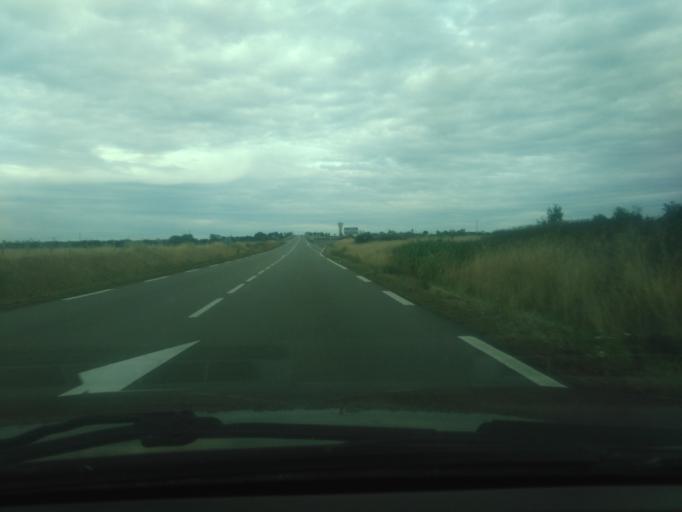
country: FR
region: Bourgogne
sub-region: Departement de la Nievre
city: Saint-Pierre-le-Moutier
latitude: 46.8020
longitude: 3.1058
